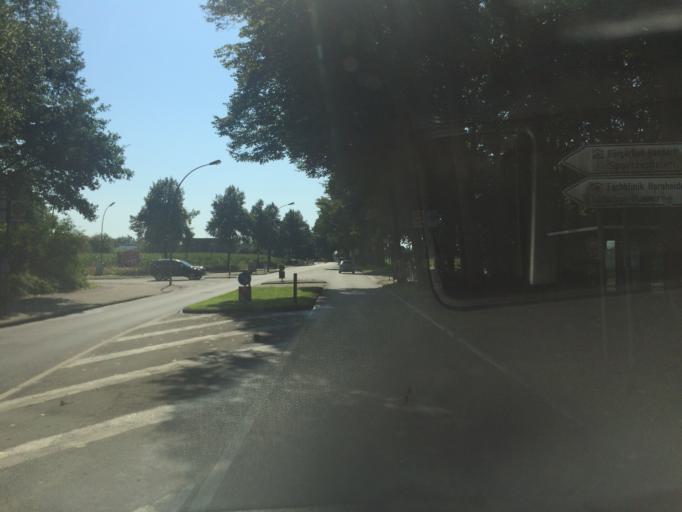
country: DE
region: North Rhine-Westphalia
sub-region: Regierungsbezirk Munster
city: Muenster
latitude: 51.9820
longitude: 7.7027
